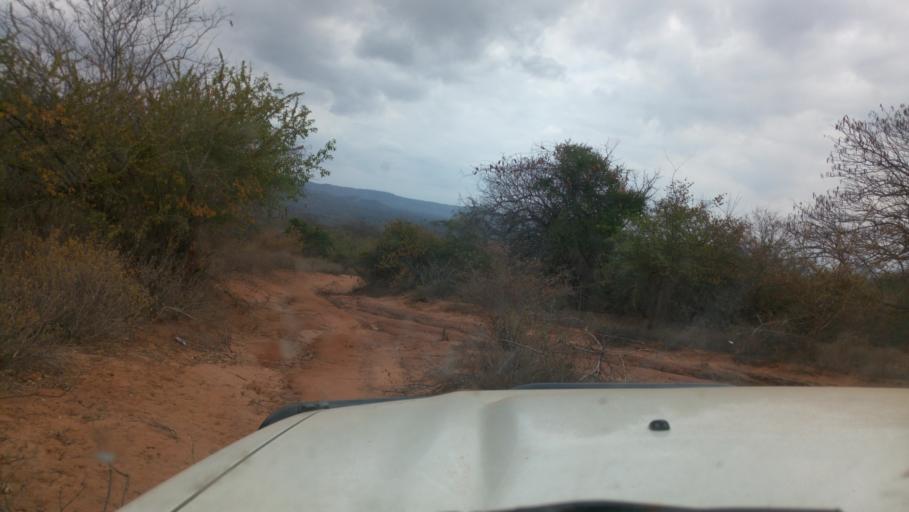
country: KE
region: Kitui
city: Kitui
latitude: -1.8465
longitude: 38.3962
